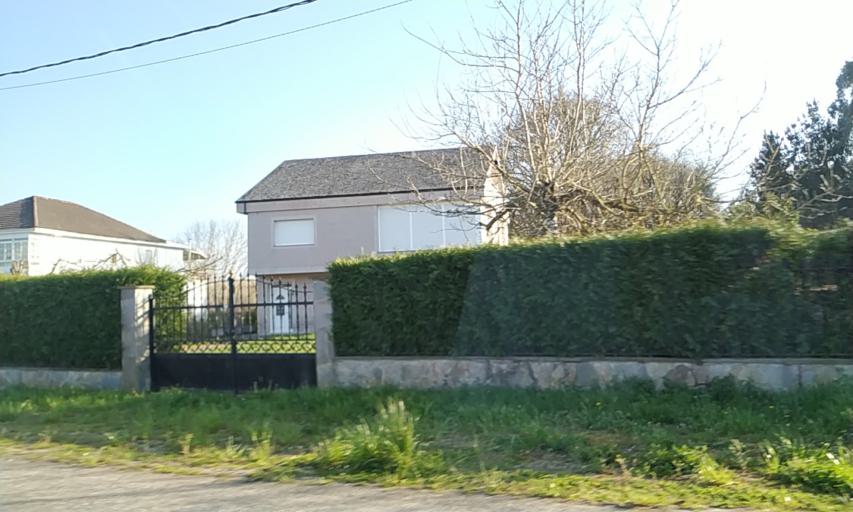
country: ES
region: Galicia
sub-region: Provincia de Lugo
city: Corgo
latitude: 42.9499
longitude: -7.4528
